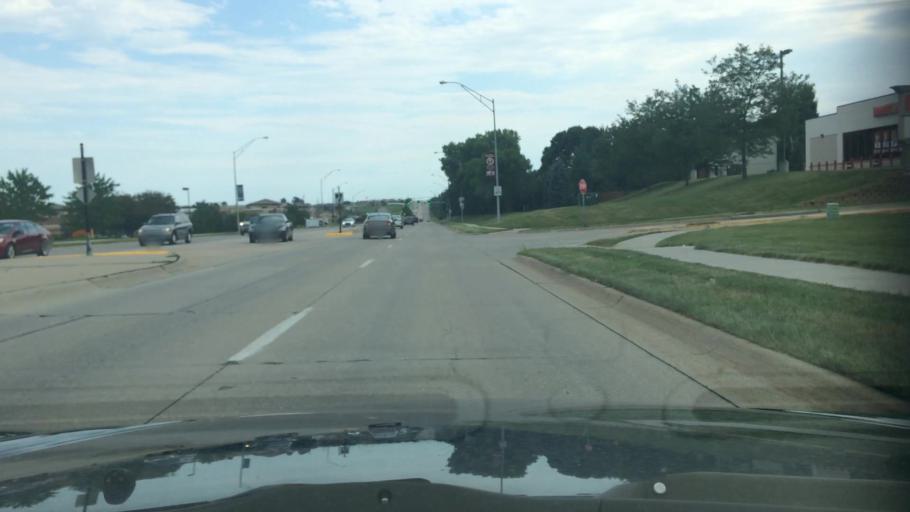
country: US
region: Nebraska
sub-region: Sarpy County
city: La Vista
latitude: 41.1754
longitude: -96.0238
